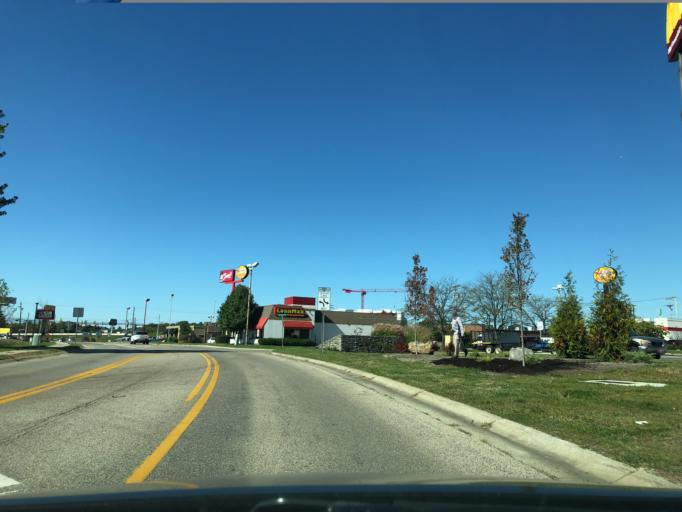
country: US
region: Ohio
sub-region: Hamilton County
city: Sixteen Mile Stand
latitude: 39.2911
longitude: -84.3132
